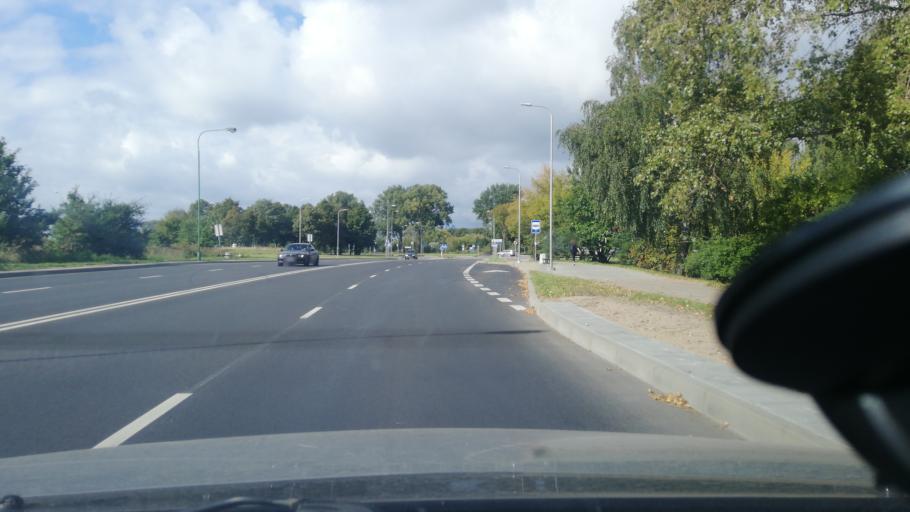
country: LT
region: Klaipedos apskritis
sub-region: Klaipeda
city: Klaipeda
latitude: 55.6657
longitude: 21.1653
